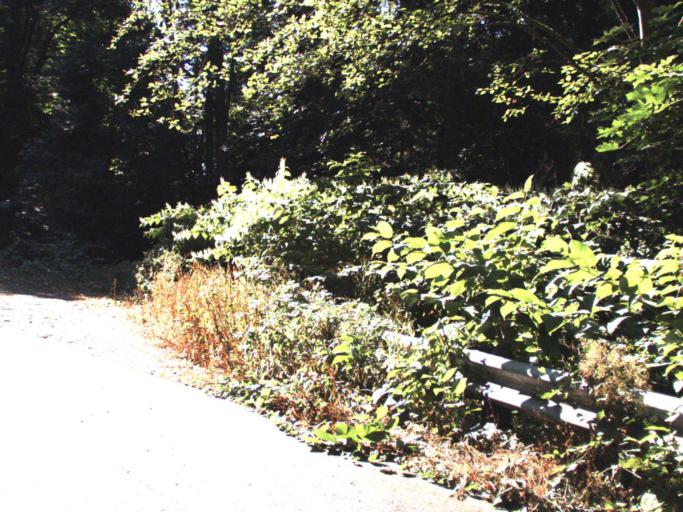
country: US
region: Washington
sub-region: Snohomish County
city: Edmonds
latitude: 47.8205
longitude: -122.3548
